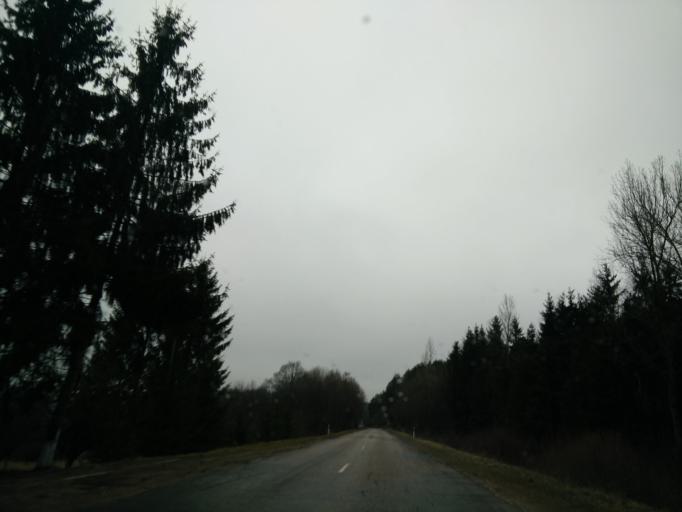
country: LT
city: Ariogala
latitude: 55.2931
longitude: 23.4426
